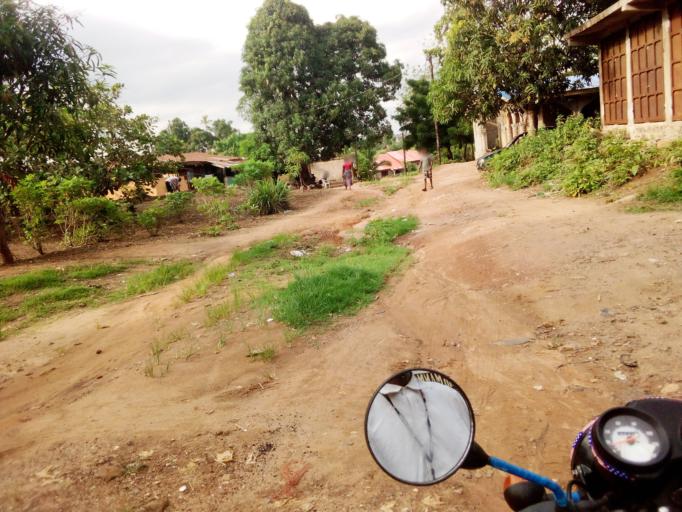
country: SL
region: Western Area
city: Waterloo
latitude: 8.3417
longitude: -13.0690
